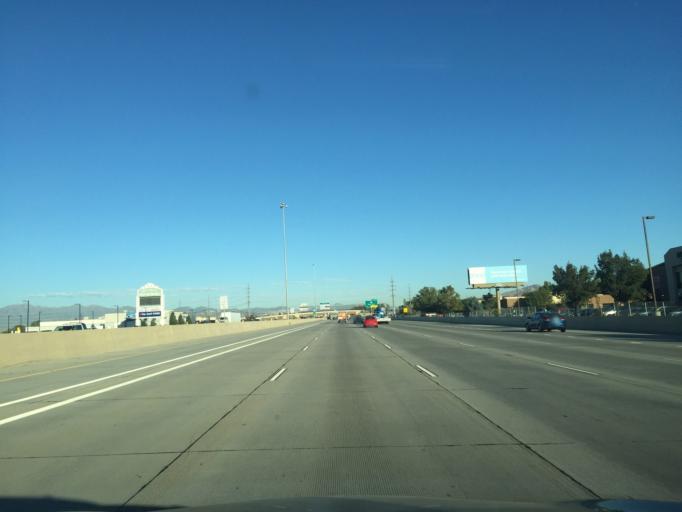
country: US
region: Utah
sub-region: Utah County
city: American Fork
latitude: 40.3565
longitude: -111.7789
